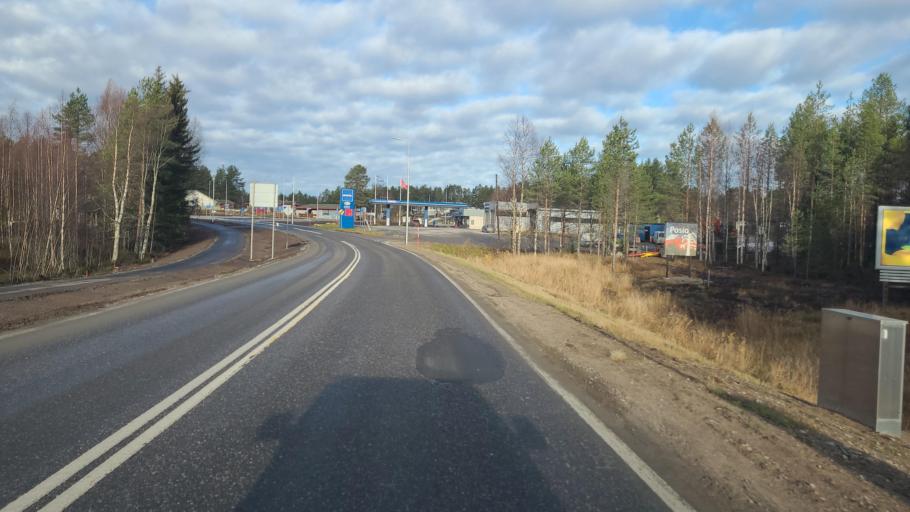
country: FI
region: Lapland
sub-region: Itae-Lappi
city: Posio
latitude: 66.1077
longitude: 28.1792
